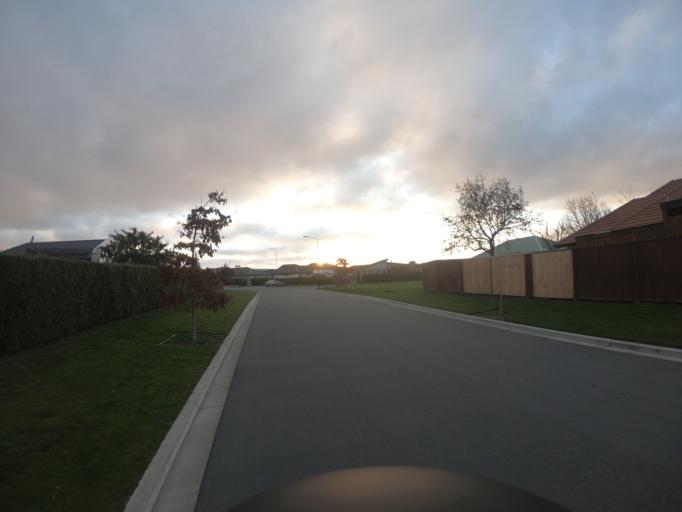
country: NZ
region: Canterbury
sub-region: Selwyn District
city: Prebbleton
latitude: -43.5652
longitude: 172.5567
